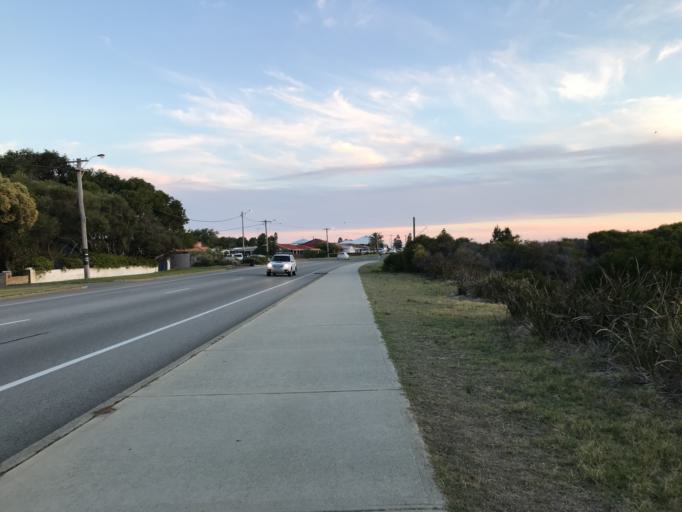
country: AU
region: Western Australia
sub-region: Rockingham
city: Shoalwater
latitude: -32.3010
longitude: 115.7039
